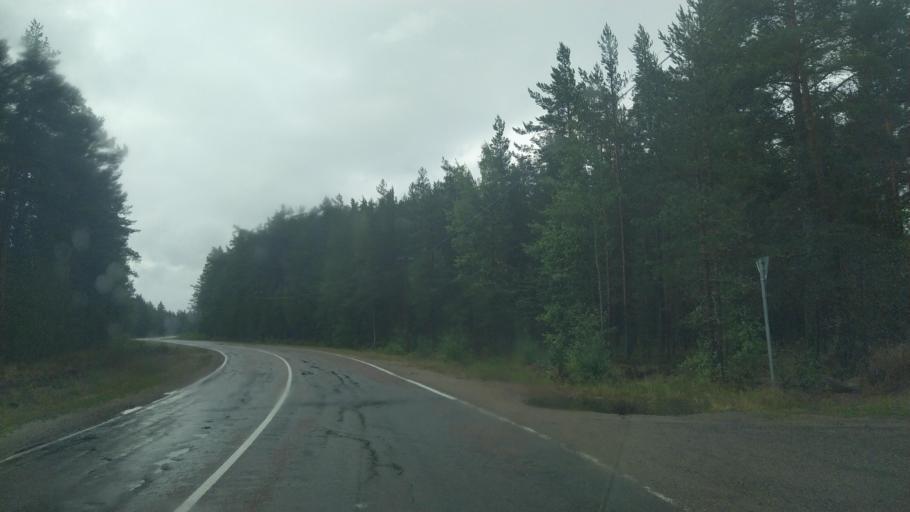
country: RU
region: Leningrad
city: Priozersk
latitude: 60.9797
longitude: 30.2707
